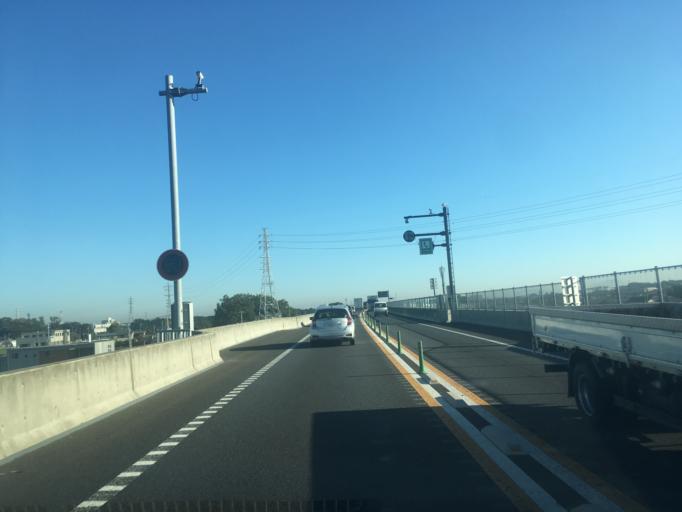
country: JP
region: Saitama
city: Kukichuo
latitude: 36.0509
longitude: 139.6865
